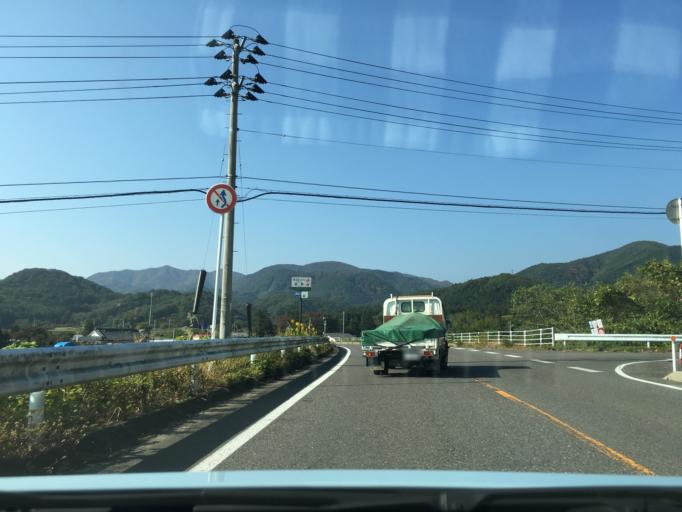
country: JP
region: Fukushima
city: Sukagawa
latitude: 37.2915
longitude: 140.1736
